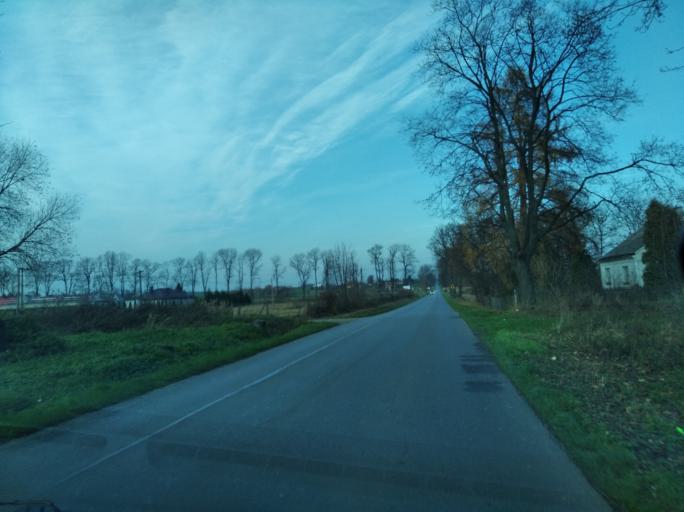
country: PL
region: Subcarpathian Voivodeship
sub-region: Powiat ropczycko-sedziszowski
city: Iwierzyce
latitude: 50.0393
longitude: 21.7460
